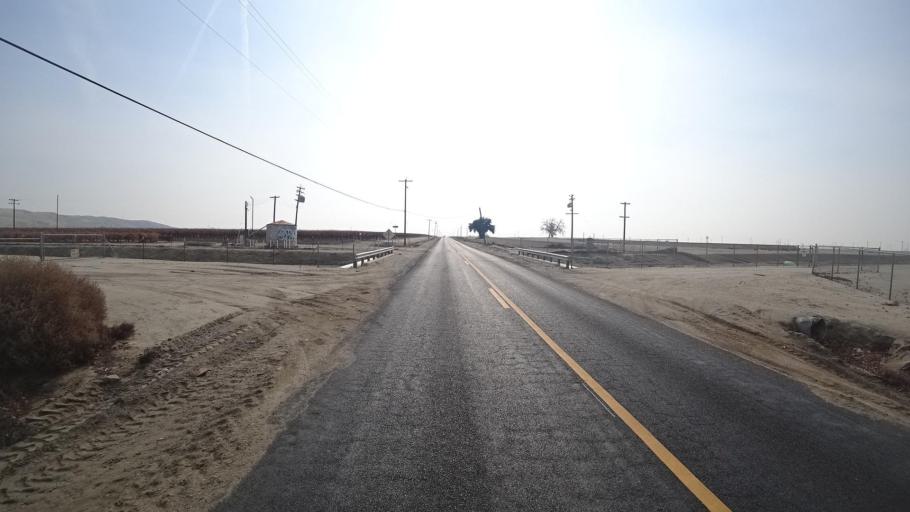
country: US
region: California
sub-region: Kern County
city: Arvin
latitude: 35.1368
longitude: -118.8507
